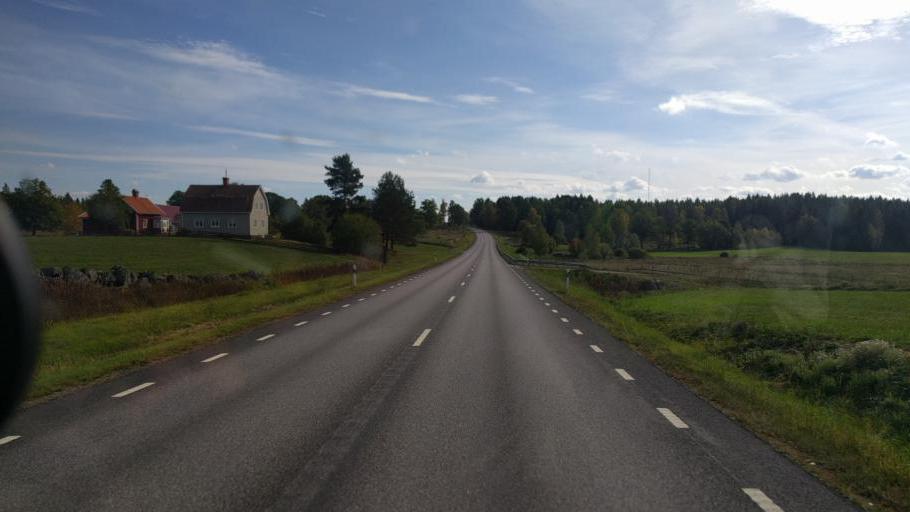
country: SE
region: OEstergoetland
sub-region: Kinda Kommun
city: Kisa
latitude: 57.9252
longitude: 15.6750
